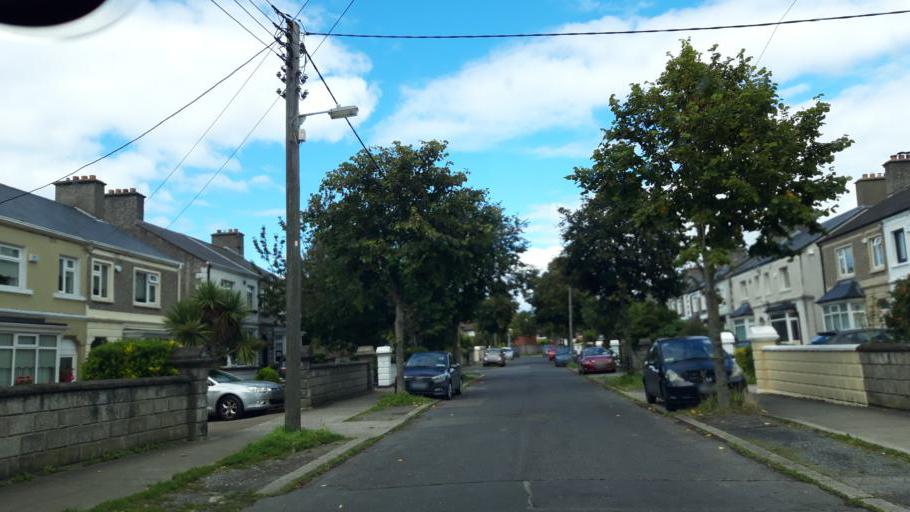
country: IE
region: Leinster
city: Dollymount
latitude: 53.3603
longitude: -6.1924
